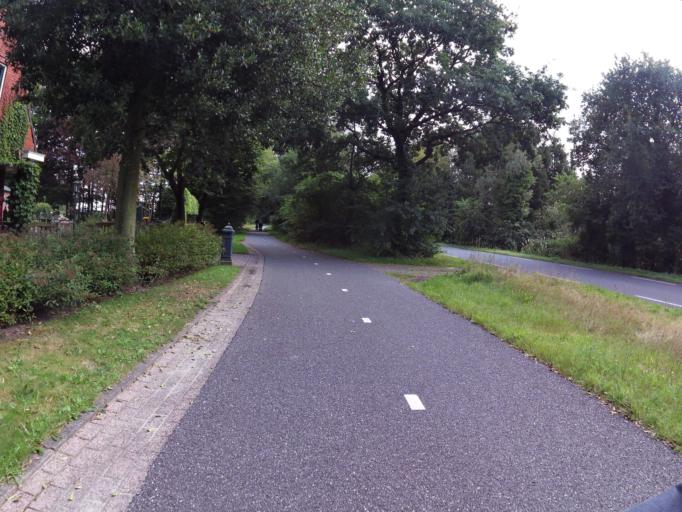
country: NL
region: Drenthe
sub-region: Gemeente Borger-Odoorn
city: Borger
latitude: 52.9332
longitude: 6.7519
